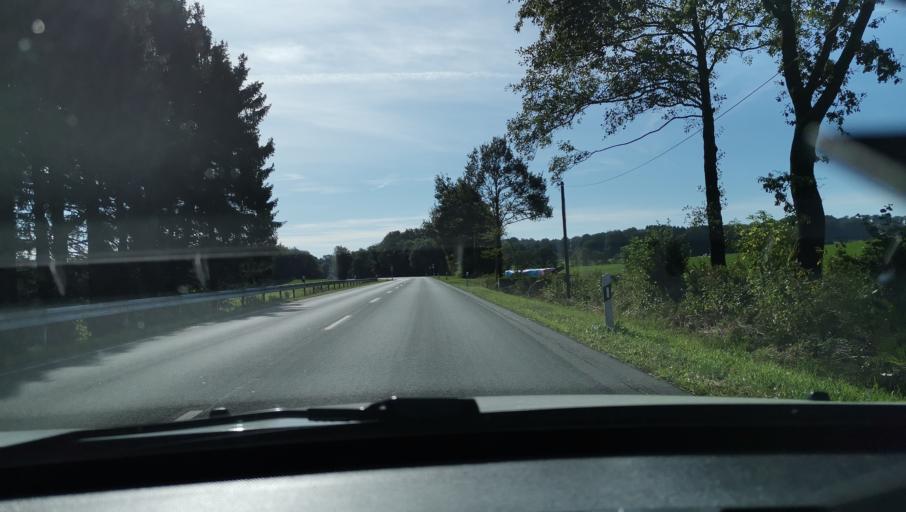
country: DE
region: North Rhine-Westphalia
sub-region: Regierungsbezirk Arnsberg
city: Breckerfeld
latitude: 51.2289
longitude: 7.4760
